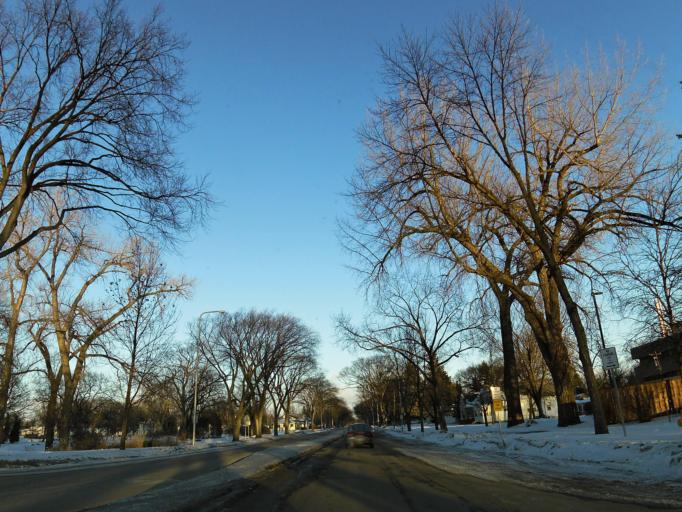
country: US
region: North Dakota
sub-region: Grand Forks County
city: Grand Forks
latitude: 47.9222
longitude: -97.0626
